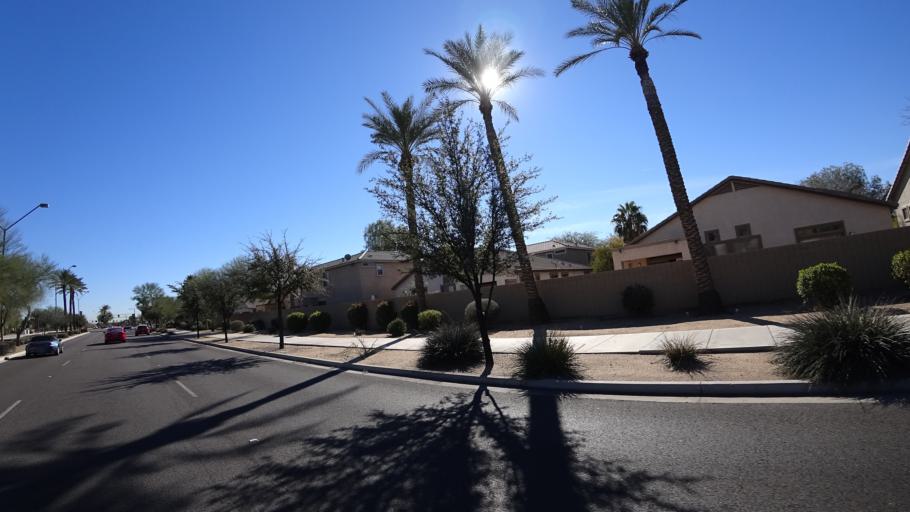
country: US
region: Arizona
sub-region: Maricopa County
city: Litchfield Park
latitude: 33.4858
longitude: -112.3673
